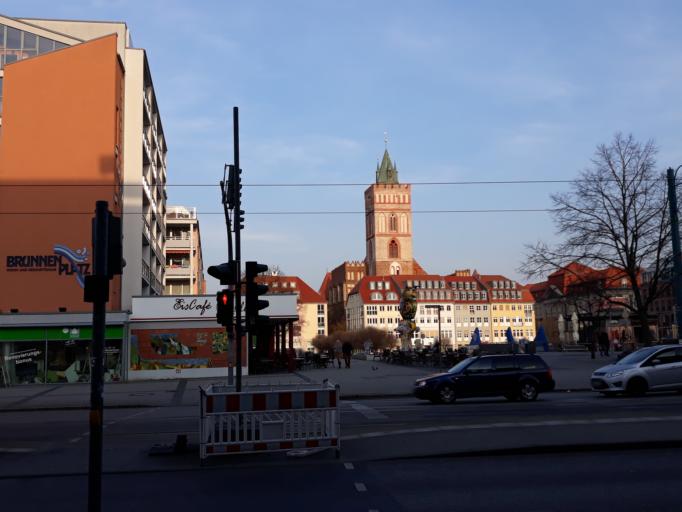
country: DE
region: Brandenburg
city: Frankfurt (Oder)
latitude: 52.3434
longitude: 14.5512
